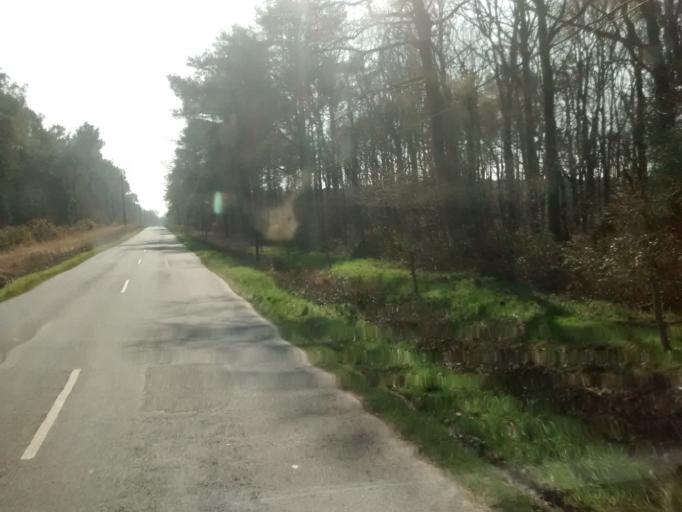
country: FR
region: Brittany
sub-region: Departement d'Ille-et-Vilaine
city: Paimpont
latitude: 48.0326
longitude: -2.1777
